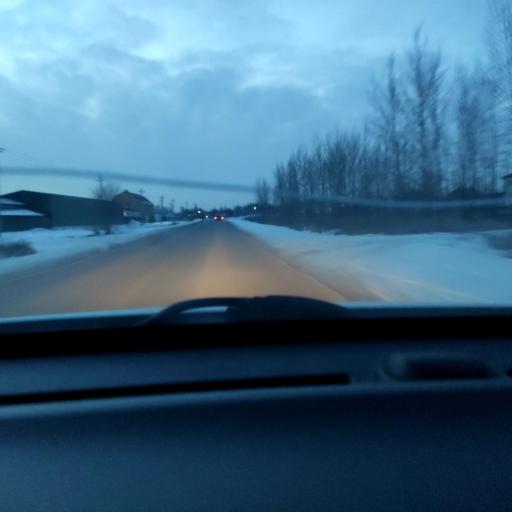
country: RU
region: Voronezj
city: Somovo
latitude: 51.6974
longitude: 39.3783
